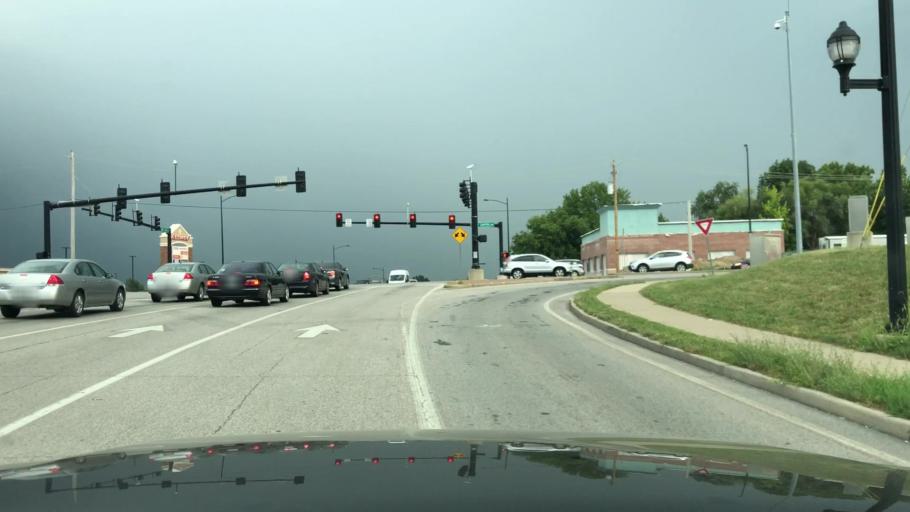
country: US
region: Missouri
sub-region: Saint Charles County
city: Saint Charles
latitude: 38.7829
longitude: -90.5057
